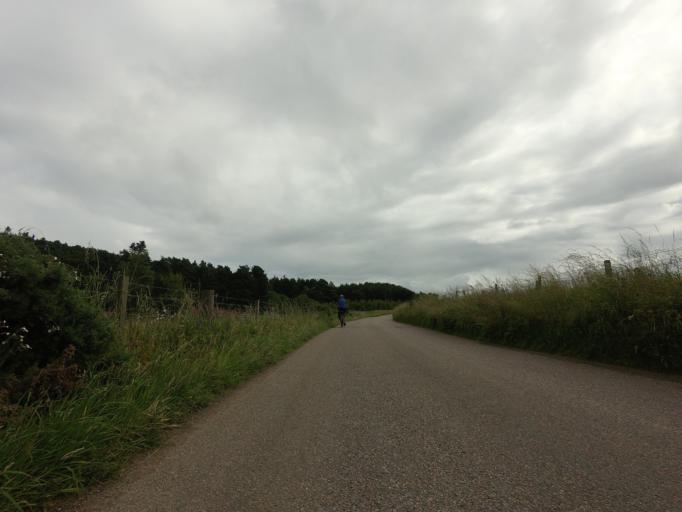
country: GB
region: Scotland
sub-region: Moray
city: Lhanbryd
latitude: 57.6676
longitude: -3.1675
